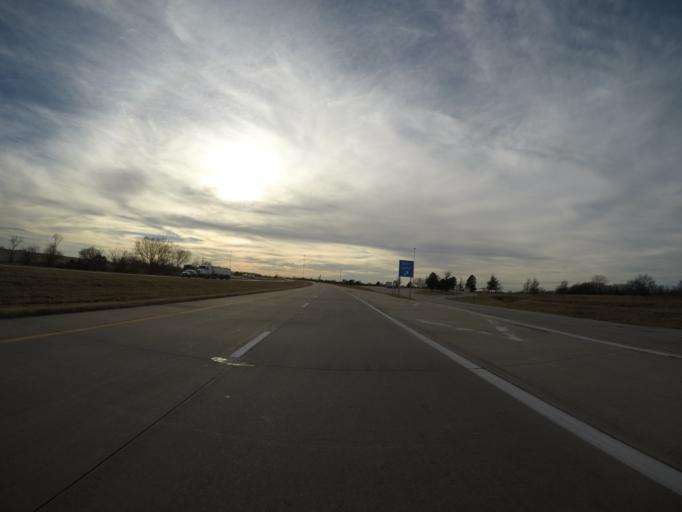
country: US
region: Kansas
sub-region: Franklin County
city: Ottawa
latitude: 38.5276
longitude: -95.4030
